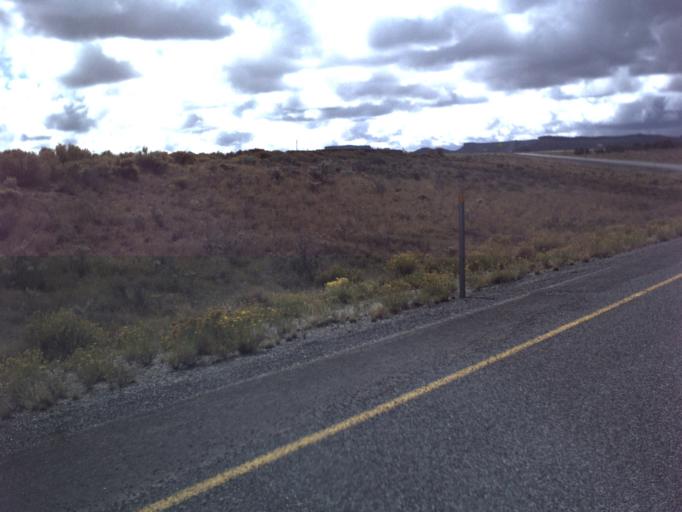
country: US
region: Utah
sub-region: Emery County
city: Castle Dale
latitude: 38.8827
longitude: -110.6574
